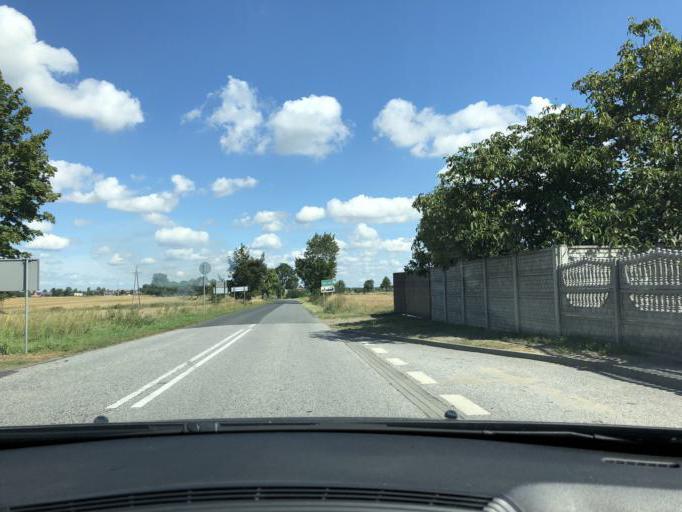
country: PL
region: Lodz Voivodeship
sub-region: Powiat wieruszowski
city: Czastary
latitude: 51.2424
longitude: 18.3169
